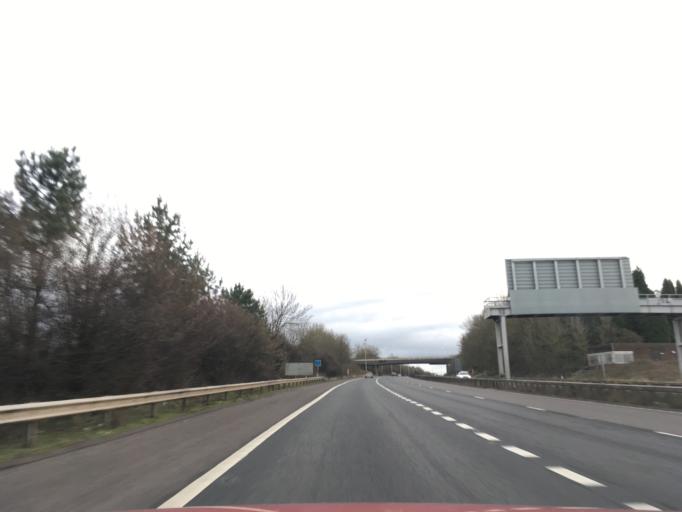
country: GB
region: England
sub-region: South Gloucestershire
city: Almondsbury
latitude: 51.5621
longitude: -2.5627
